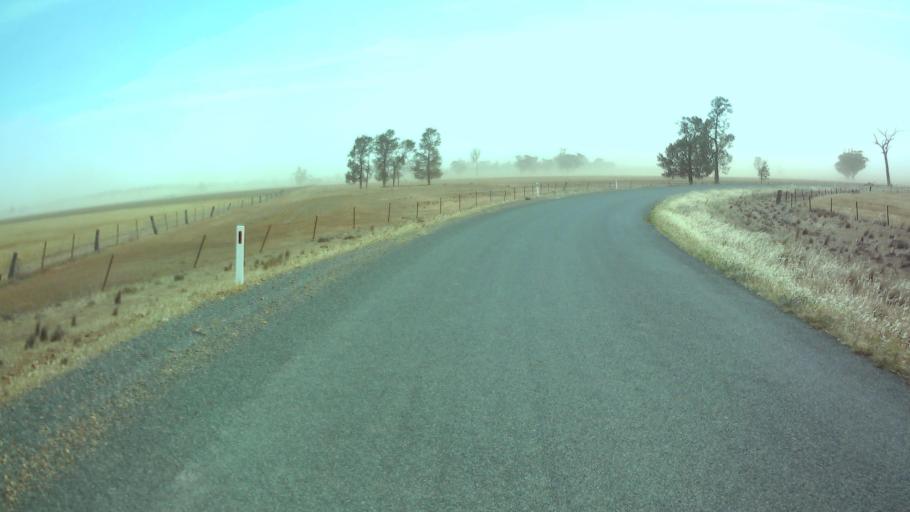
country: AU
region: New South Wales
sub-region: Weddin
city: Grenfell
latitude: -33.7379
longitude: 147.9932
